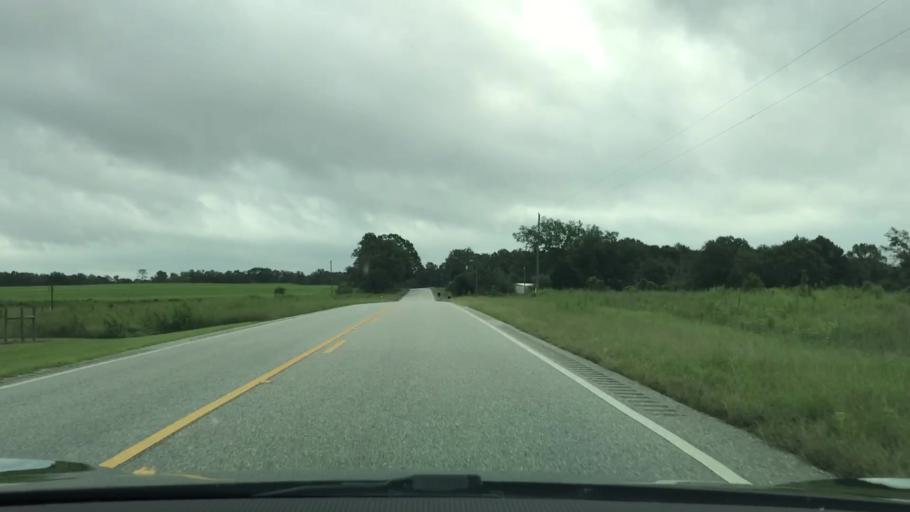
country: US
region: Alabama
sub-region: Geneva County
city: Samson
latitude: 31.0242
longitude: -86.1183
